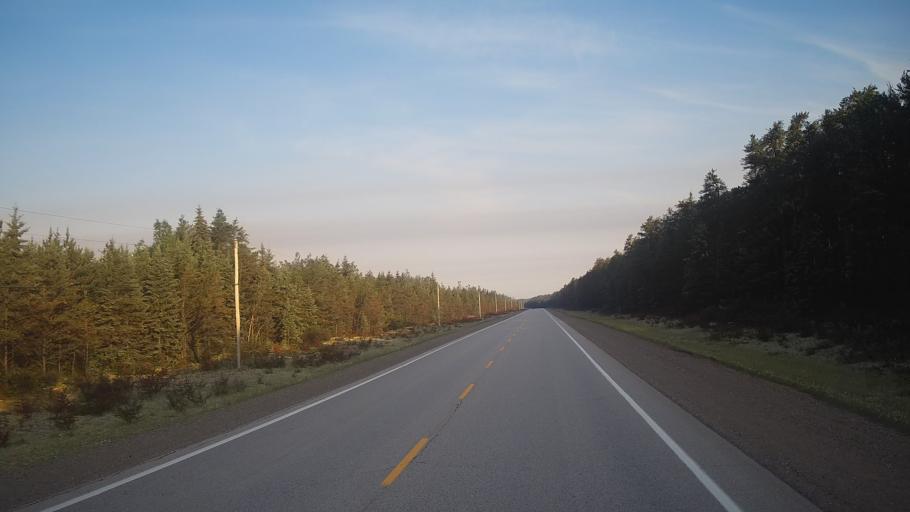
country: CA
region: Ontario
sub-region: Rainy River District
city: Atikokan
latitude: 49.2435
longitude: -91.0219
